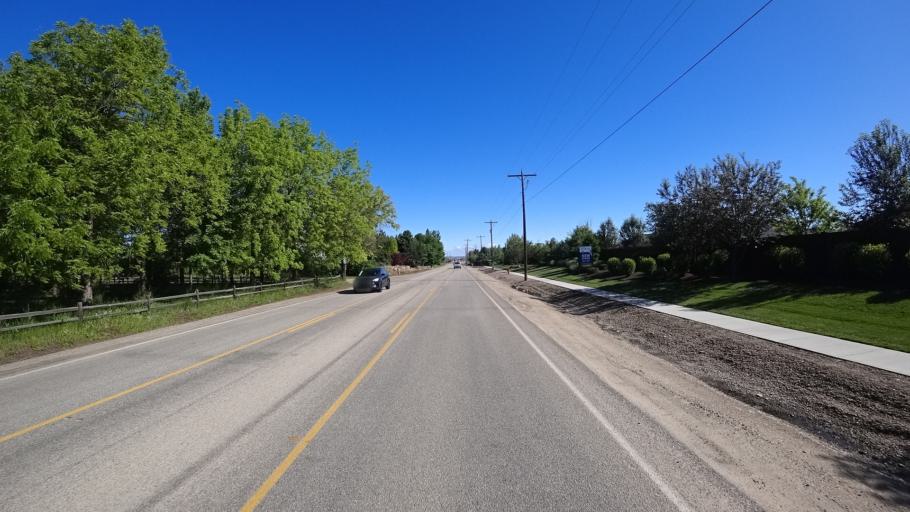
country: US
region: Idaho
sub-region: Ada County
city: Star
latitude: 43.6591
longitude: -116.4536
